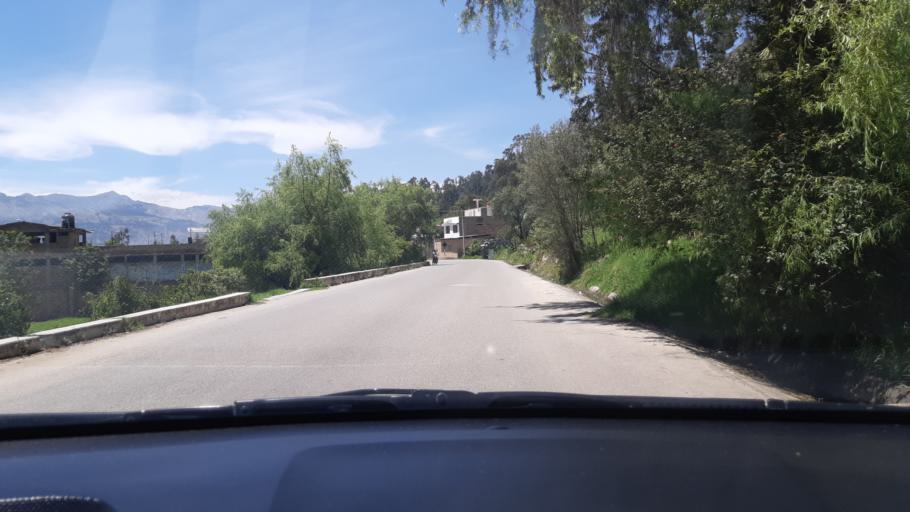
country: PE
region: Cajamarca
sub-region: Provincia de Cajamarca
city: Llacanora
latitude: -7.1833
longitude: -78.4451
